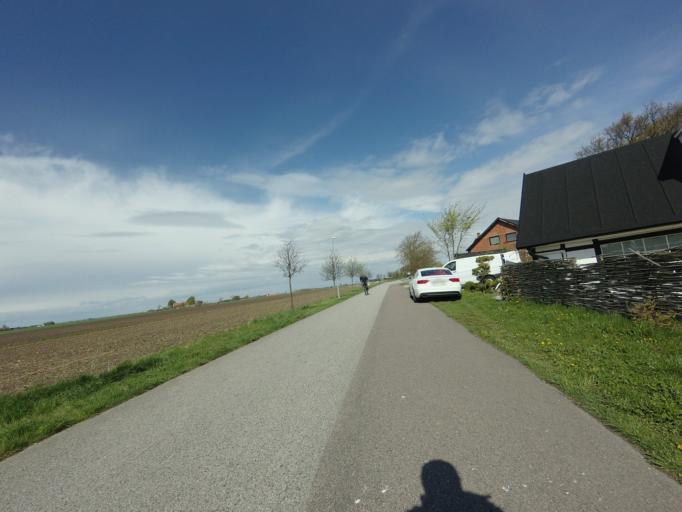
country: SE
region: Skane
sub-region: Vellinge Kommun
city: Vellinge
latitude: 55.4896
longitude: 13.0077
